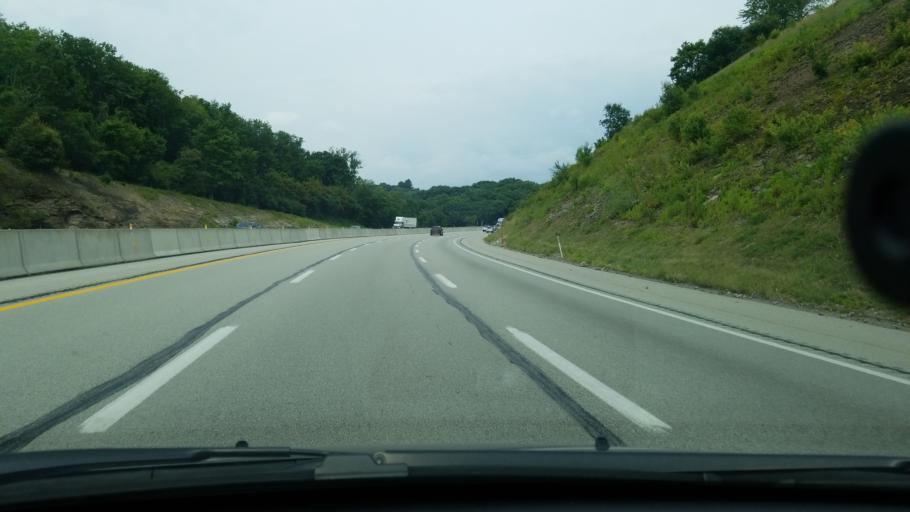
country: US
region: Pennsylvania
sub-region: Butler County
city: Mars
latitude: 40.6442
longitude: -80.0204
